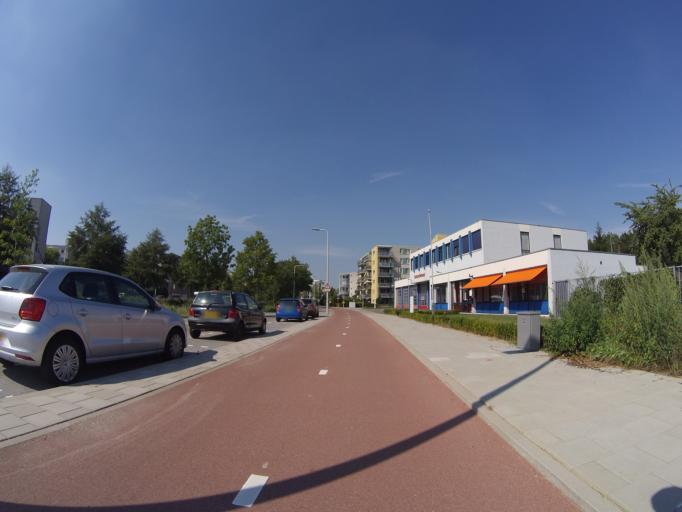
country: NL
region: Utrecht
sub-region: Gemeente Utrecht
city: Utrecht
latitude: 52.1058
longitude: 5.1444
